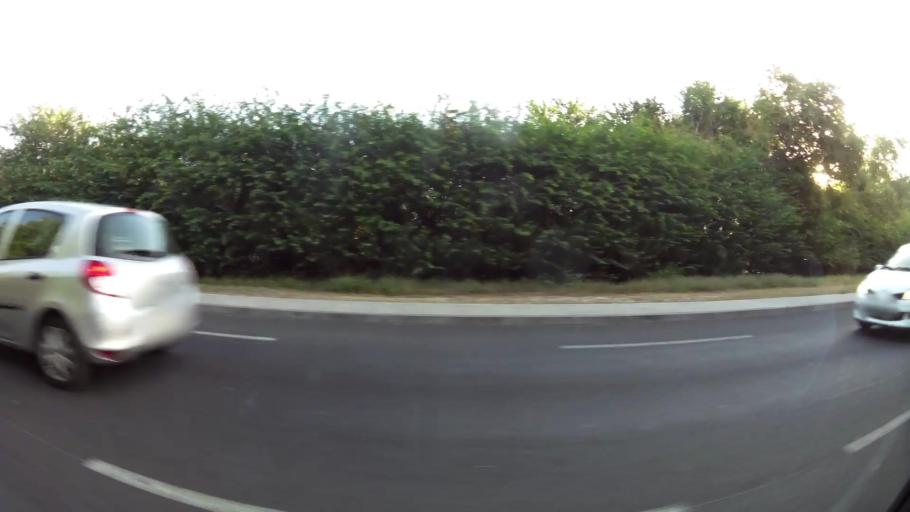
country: RE
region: Reunion
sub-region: Reunion
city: Trois-Bassins
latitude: -21.0855
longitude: 55.2323
